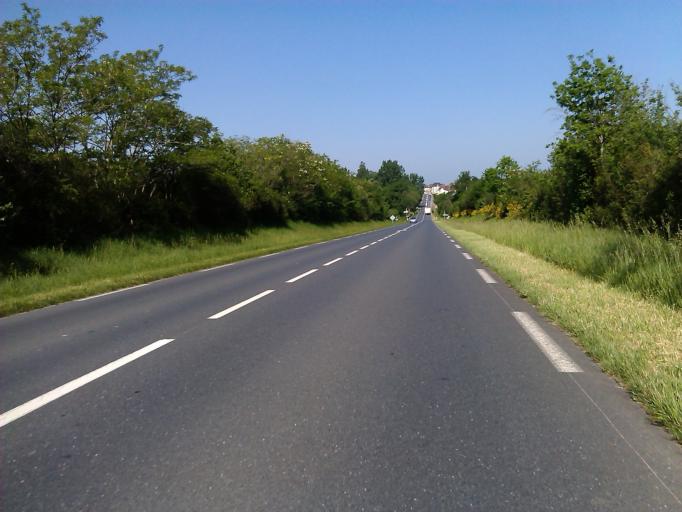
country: FR
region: Centre
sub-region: Departement de l'Indre
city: Arthon
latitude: 46.6129
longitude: 1.6939
